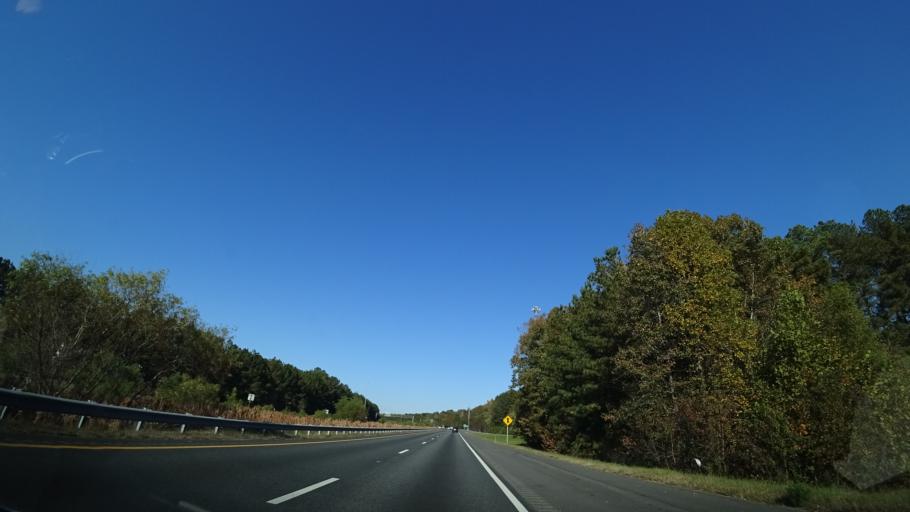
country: US
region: Virginia
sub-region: City of Portsmouth
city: Portsmouth Heights
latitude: 36.8503
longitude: -76.4322
